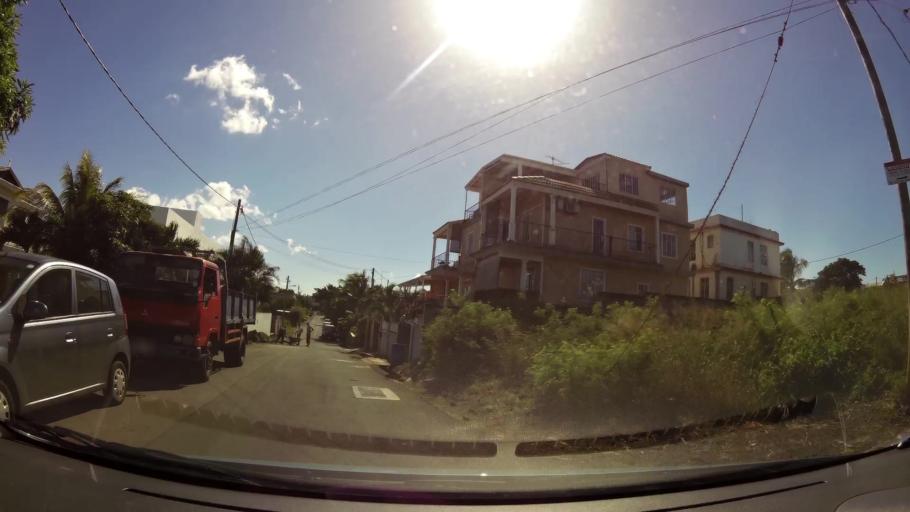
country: MU
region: Black River
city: Flic en Flac
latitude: -20.2783
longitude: 57.3758
